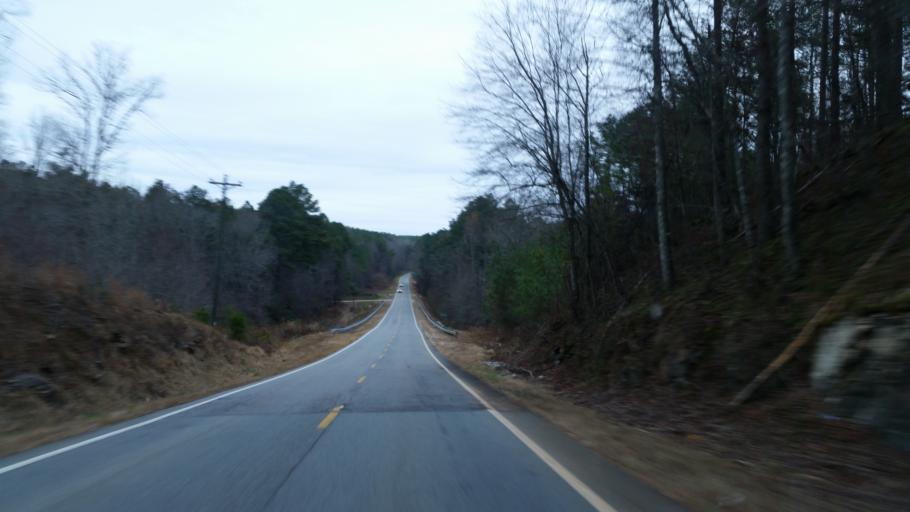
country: US
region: Georgia
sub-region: Dawson County
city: Dawsonville
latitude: 34.4520
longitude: -84.1279
